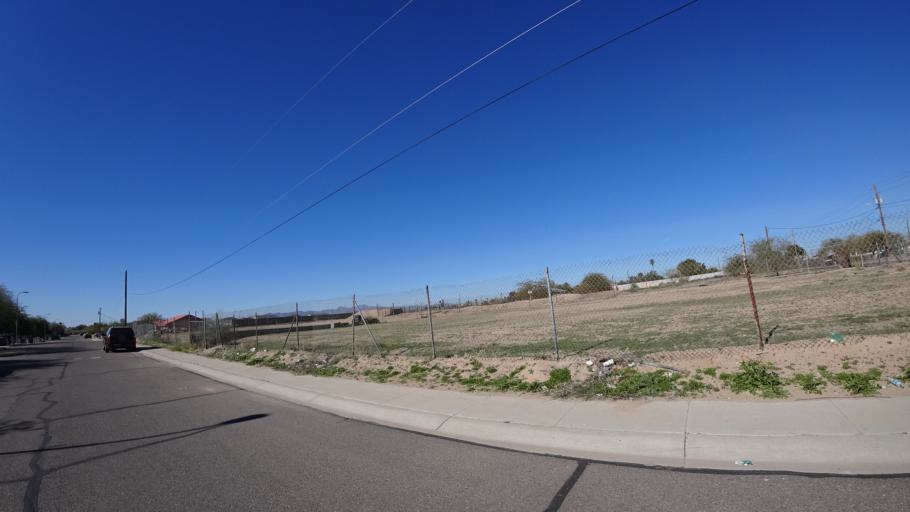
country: US
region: Arizona
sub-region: Maricopa County
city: Avondale
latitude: 33.4143
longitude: -112.3280
